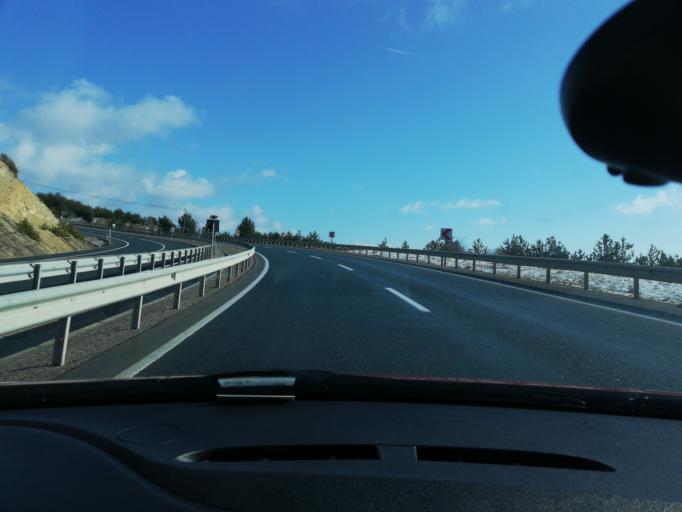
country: TR
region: Kastamonu
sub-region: Cide
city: Kastamonu
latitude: 41.3644
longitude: 33.7584
